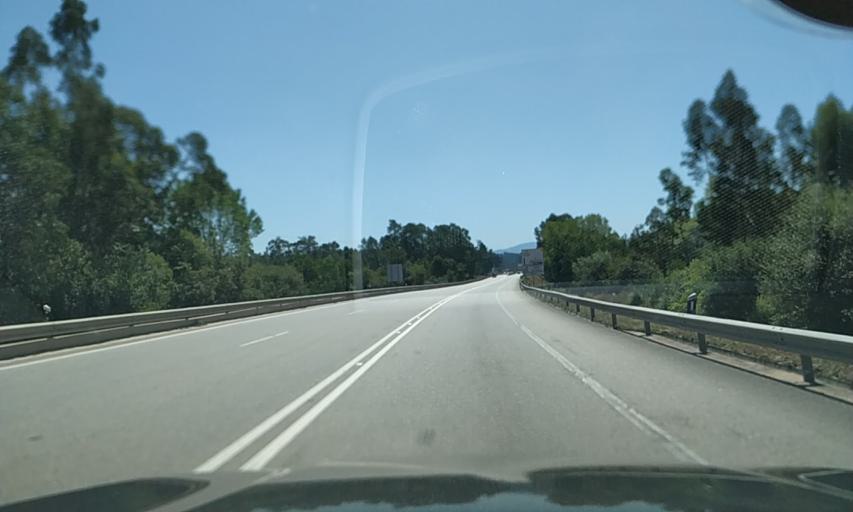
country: PT
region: Aveiro
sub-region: Agueda
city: Aguada de Cima
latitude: 40.5292
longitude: -8.4547
